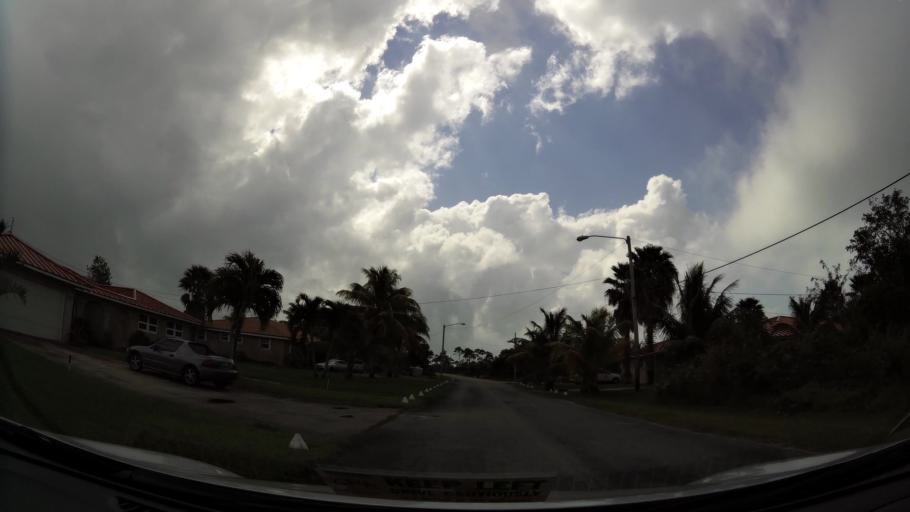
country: BS
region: Freeport
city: Lucaya
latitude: 26.5428
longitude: -78.5935
